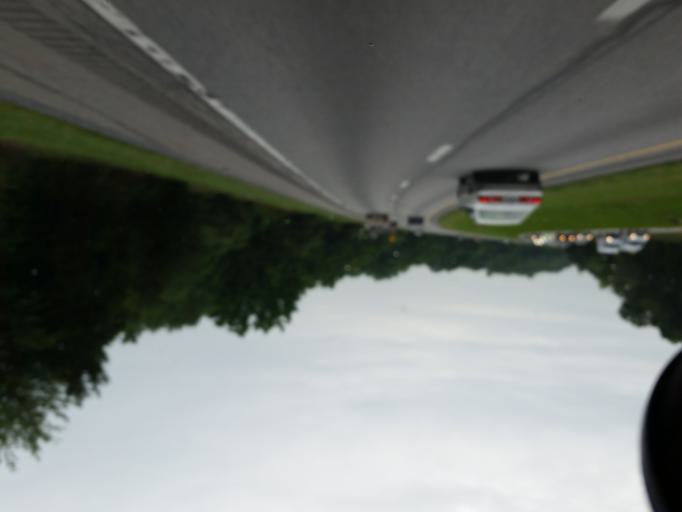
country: US
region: Pennsylvania
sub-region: Dauphin County
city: Middletown
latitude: 40.2028
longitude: -76.7036
